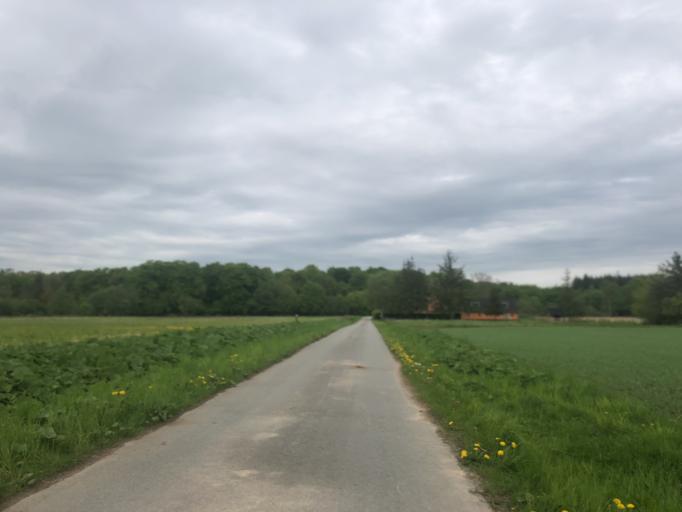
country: DK
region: Zealand
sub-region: Koge Kommune
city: Bjaeverskov
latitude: 55.4304
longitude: 12.0809
